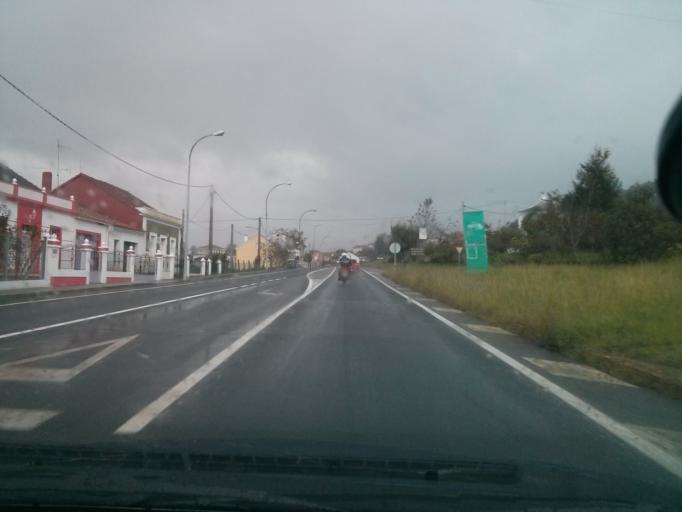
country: ES
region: Galicia
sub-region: Provincia da Coruna
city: Noia
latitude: 42.8039
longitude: -8.8842
